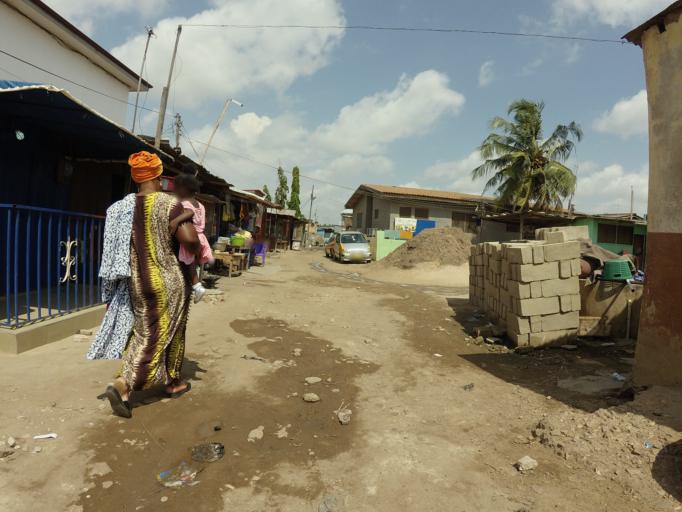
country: GH
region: Greater Accra
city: Dome
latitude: 5.6177
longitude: -0.2493
